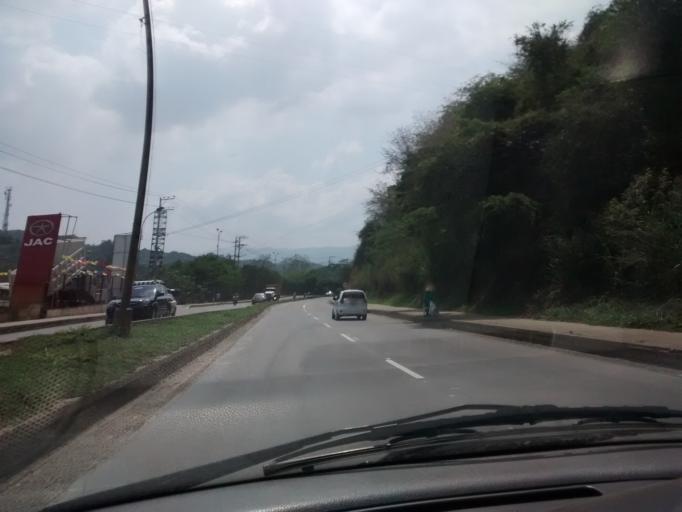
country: CO
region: Santander
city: Bucaramanga
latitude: 7.0904
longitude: -73.1299
